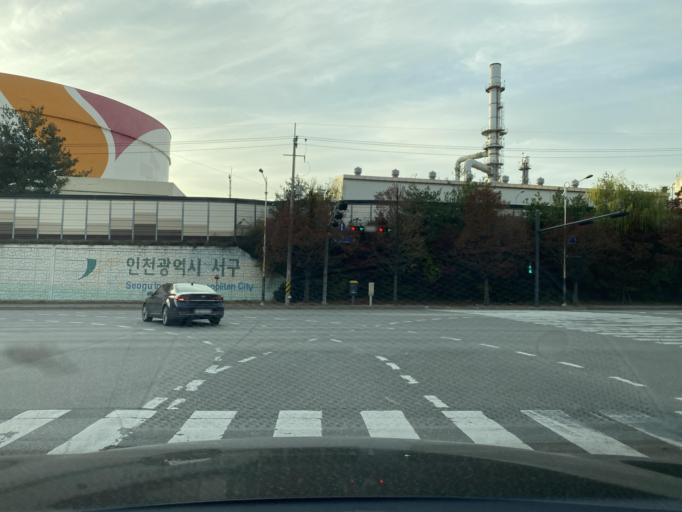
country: KR
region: Incheon
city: Incheon
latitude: 37.5069
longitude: 126.6621
